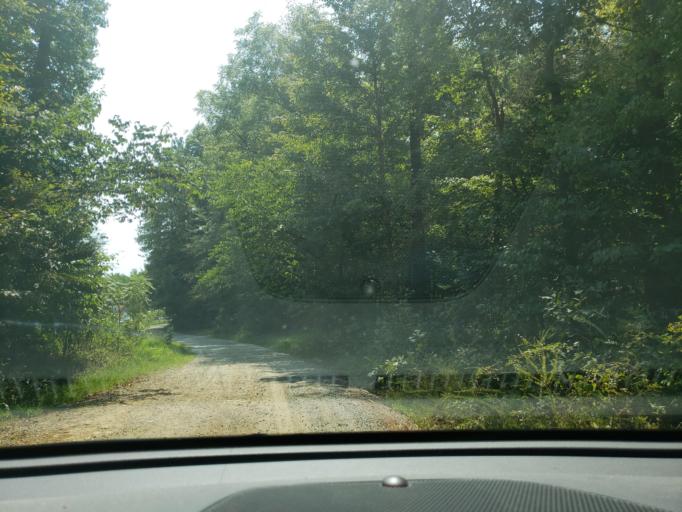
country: US
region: North Carolina
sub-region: Orange County
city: Hillsborough
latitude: 36.0056
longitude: -79.0848
